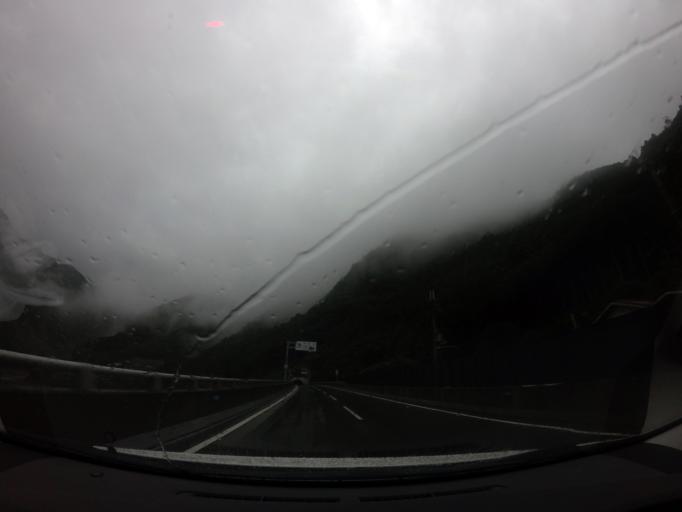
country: JP
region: Wakayama
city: Shingu
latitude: 33.9523
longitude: 135.8009
